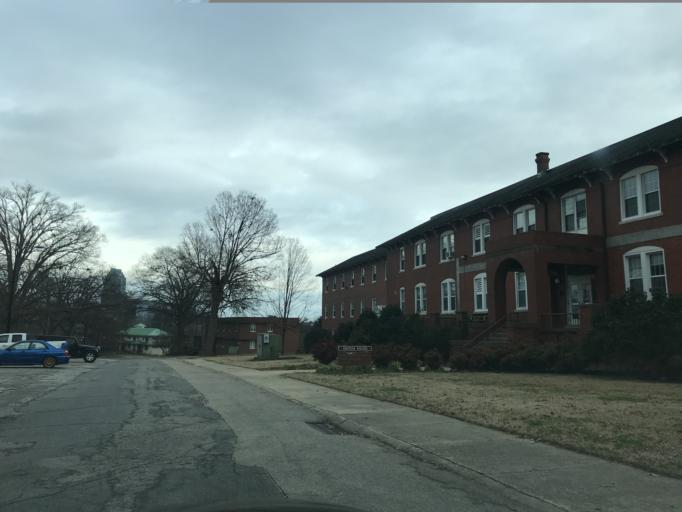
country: US
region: North Carolina
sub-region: Wake County
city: Raleigh
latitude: 35.7675
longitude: -78.6527
